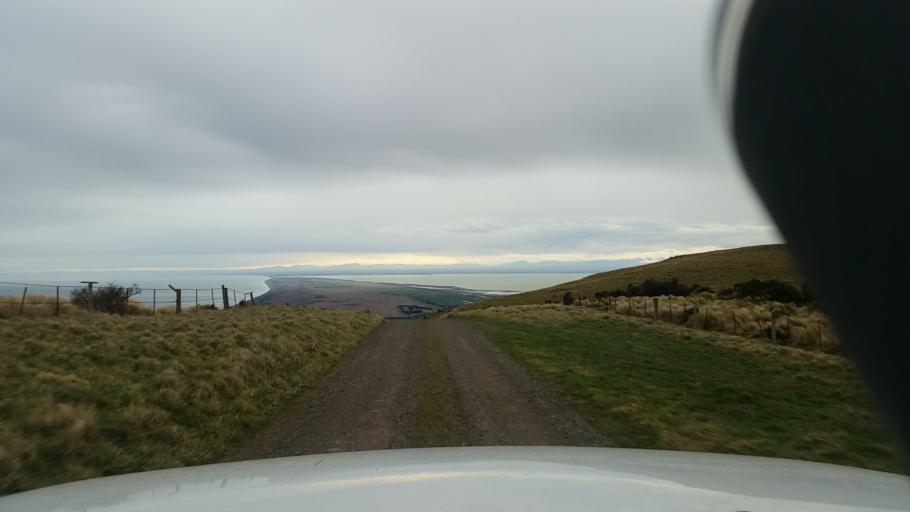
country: NZ
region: Canterbury
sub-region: Christchurch City
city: Christchurch
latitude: -43.8157
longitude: 172.7591
